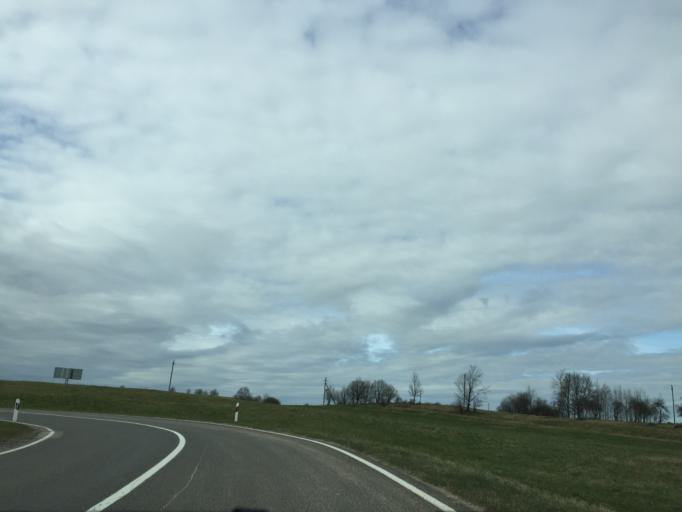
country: LT
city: Silale
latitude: 55.5878
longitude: 22.1435
